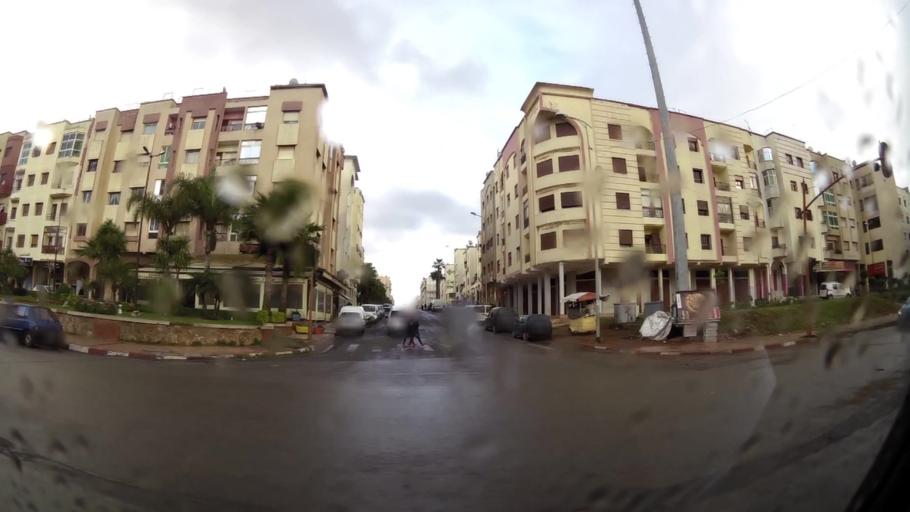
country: MA
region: Grand Casablanca
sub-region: Mohammedia
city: Mohammedia
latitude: 33.6787
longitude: -7.3868
